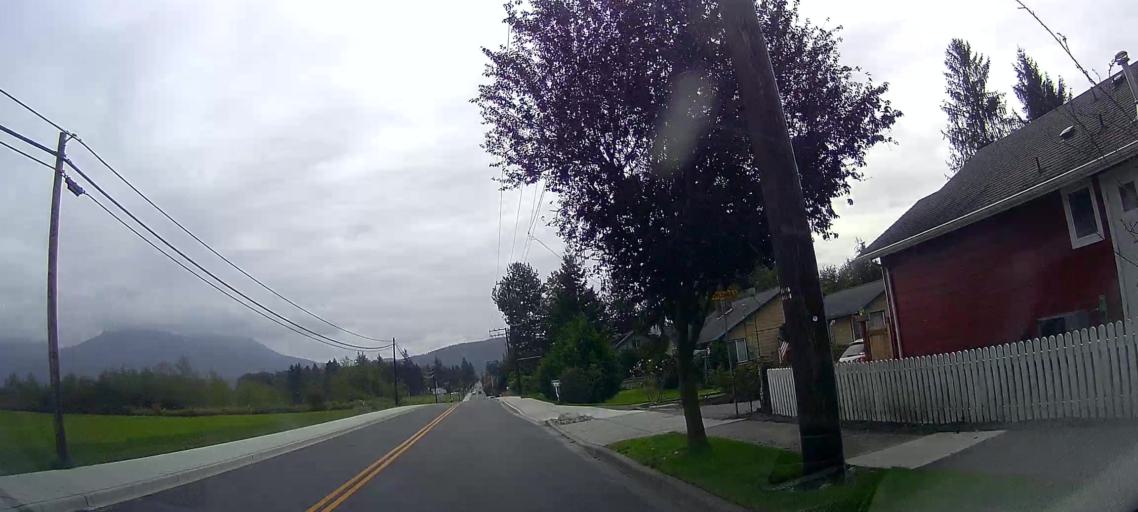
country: US
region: Washington
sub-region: Skagit County
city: Sedro-Woolley
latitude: 48.5257
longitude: -122.2107
